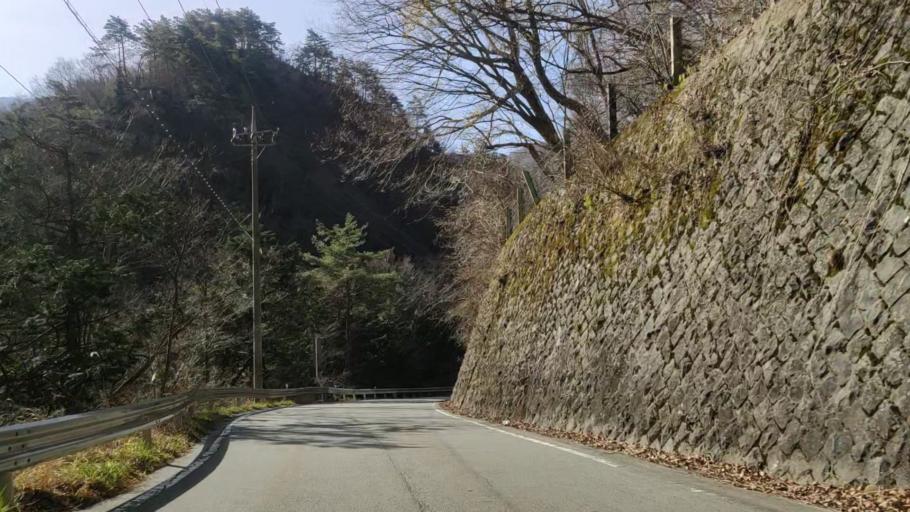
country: JP
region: Yamanashi
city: Fujikawaguchiko
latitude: 35.5336
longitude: 138.6224
